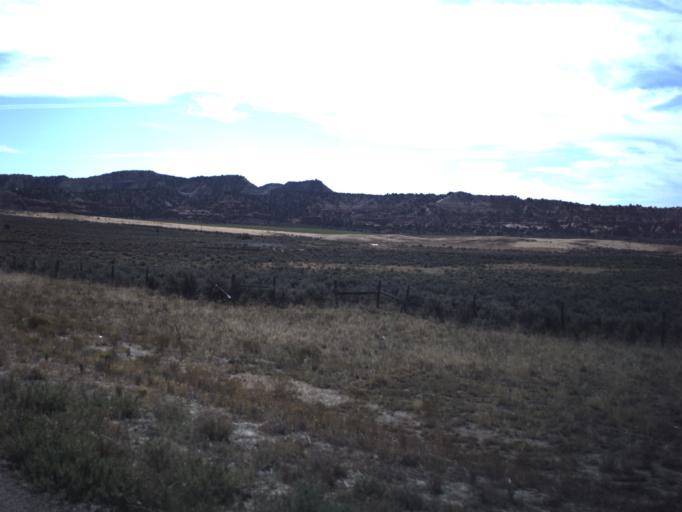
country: US
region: Utah
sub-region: Garfield County
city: Panguitch
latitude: 37.5616
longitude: -112.0295
